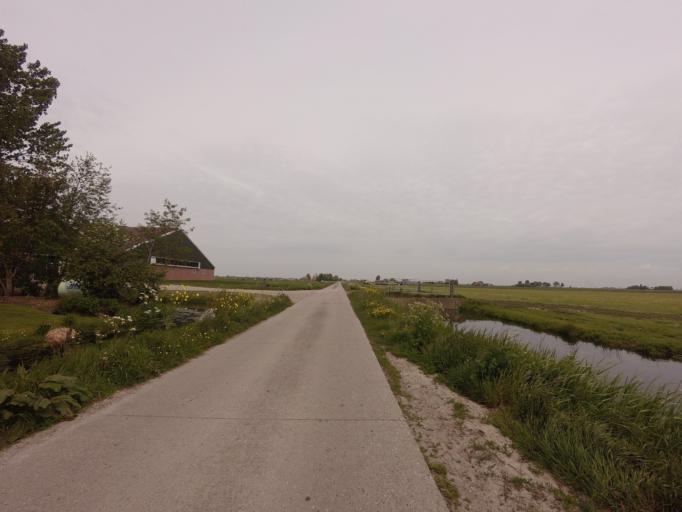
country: NL
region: Friesland
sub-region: Sudwest Fryslan
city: Workum
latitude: 53.0187
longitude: 5.4603
